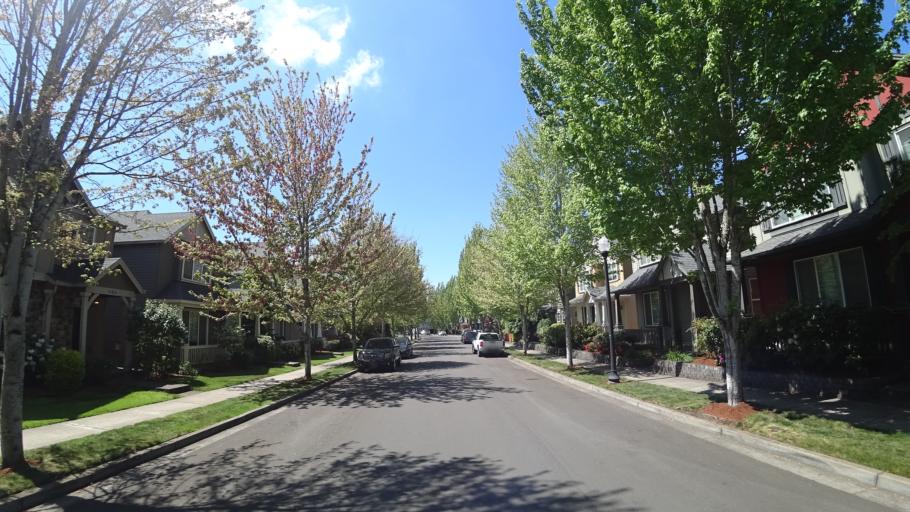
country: US
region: Oregon
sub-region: Washington County
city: Hillsboro
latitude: 45.5086
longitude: -122.9730
